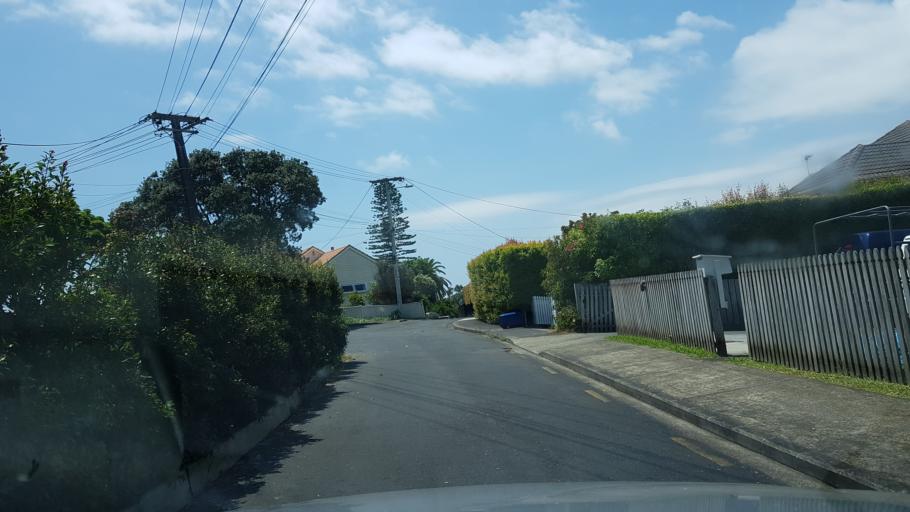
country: NZ
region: Auckland
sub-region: Auckland
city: North Shore
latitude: -36.8150
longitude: 174.7971
